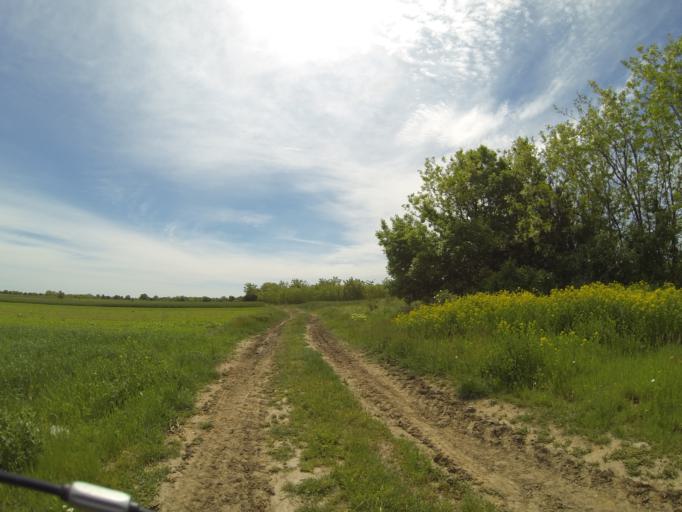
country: RO
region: Dolj
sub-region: Comuna Leu
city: Leu
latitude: 44.1986
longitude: 23.9877
